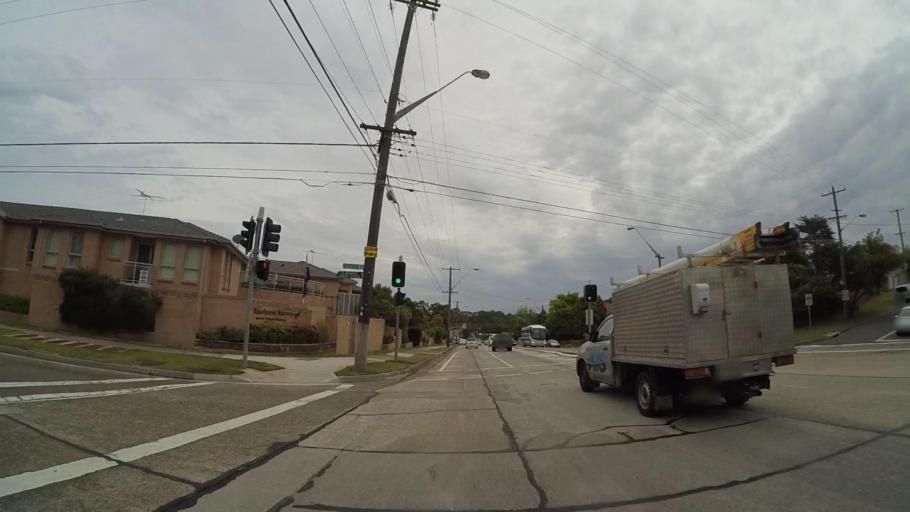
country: AU
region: New South Wales
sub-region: Kogarah
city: Kogarah
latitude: -33.9840
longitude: 151.1141
